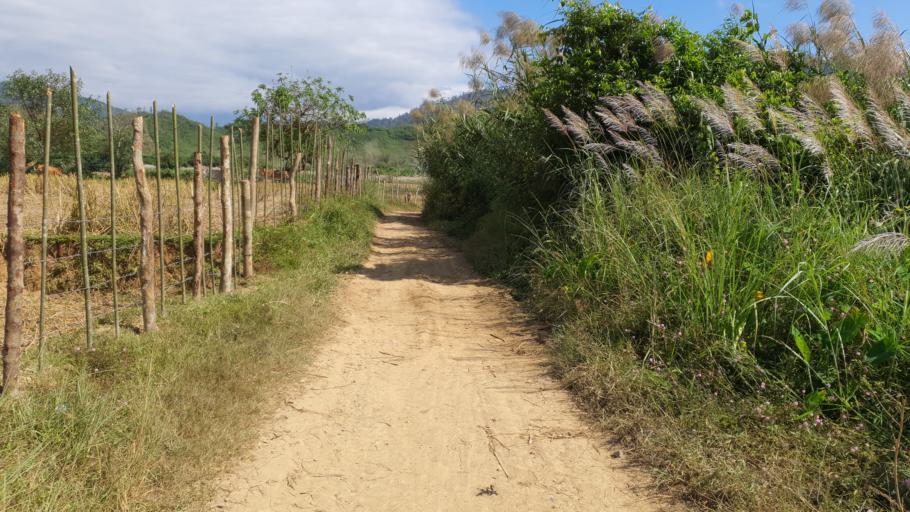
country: LA
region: Bolikhamxai
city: Bolikhan
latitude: 18.9065
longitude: 103.7423
